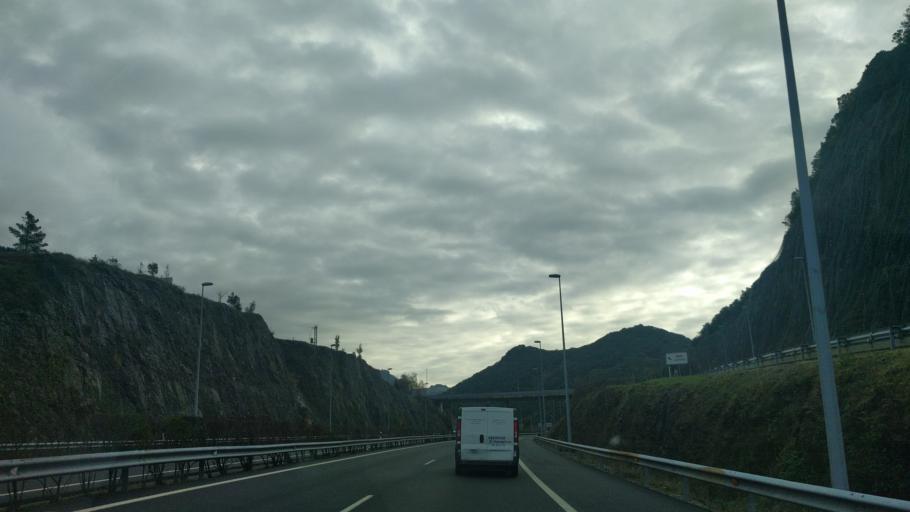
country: ES
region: Cantabria
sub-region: Provincia de Cantabria
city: Liendo
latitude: 43.3909
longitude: -3.3535
